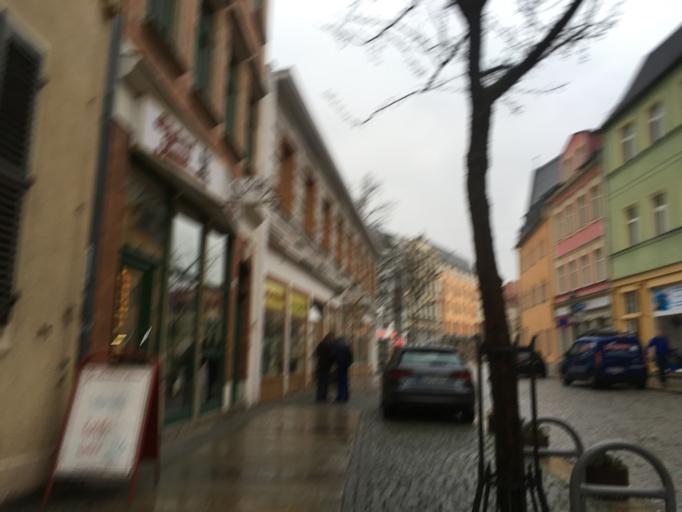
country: DE
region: Saxony
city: Zwickau
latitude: 50.7173
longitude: 12.4959
